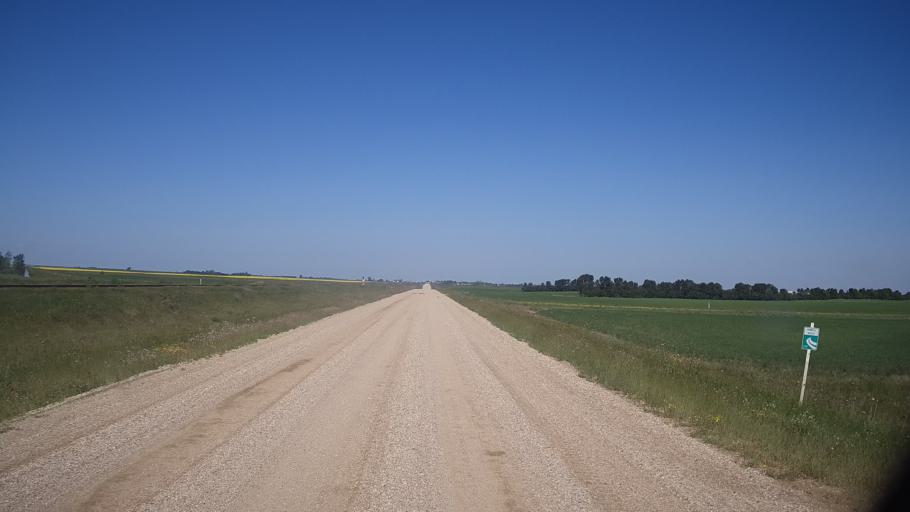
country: CA
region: Saskatchewan
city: Watrous
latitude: 51.8748
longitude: -106.0044
